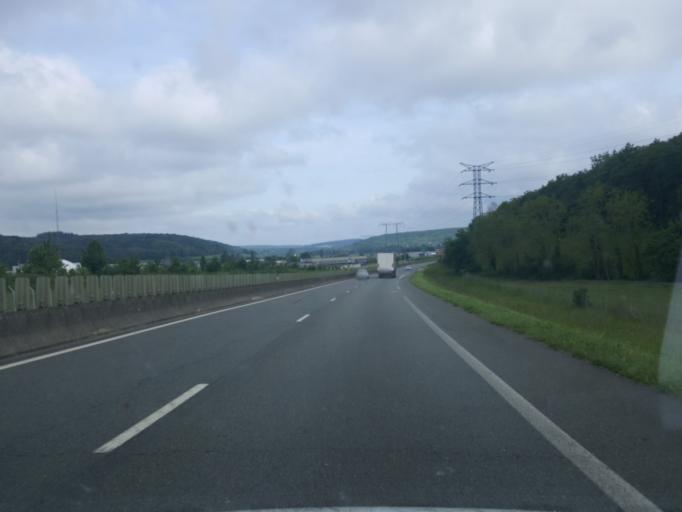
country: FR
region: Haute-Normandie
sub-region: Departement de l'Eure
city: Gravigny
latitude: 49.0527
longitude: 1.1780
